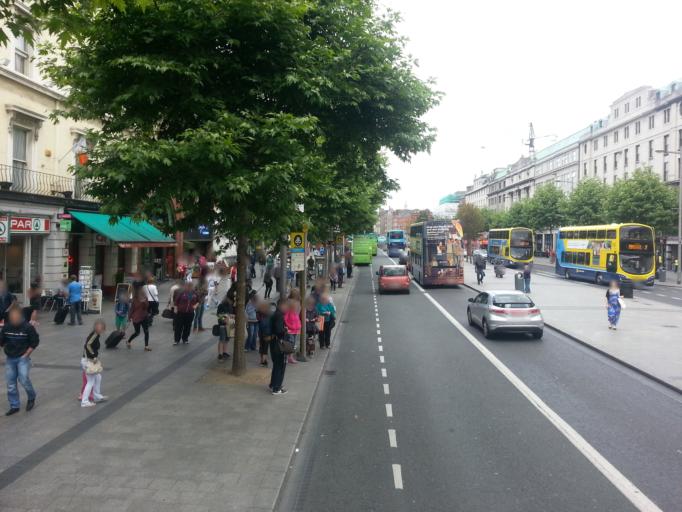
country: IE
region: Leinster
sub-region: Dublin City
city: Dublin
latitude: 53.3500
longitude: -6.2605
